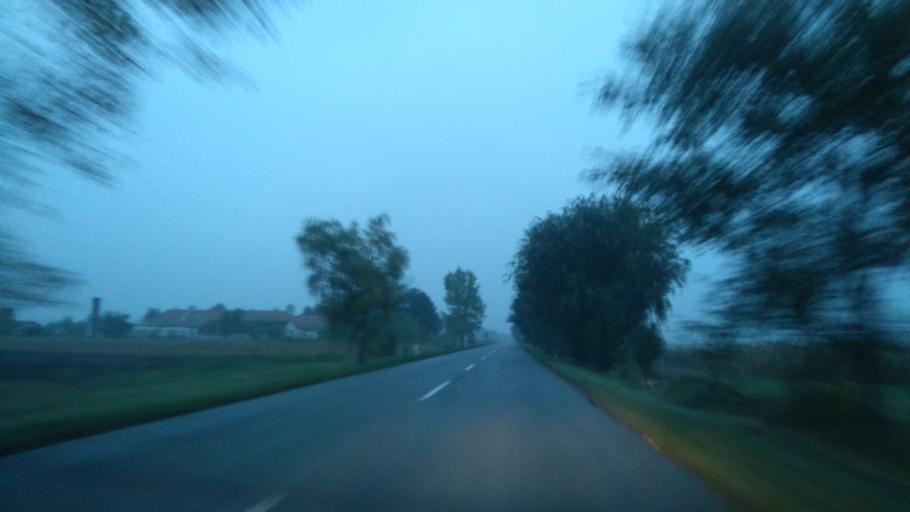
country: RS
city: Mol
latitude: 45.7452
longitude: 20.1217
